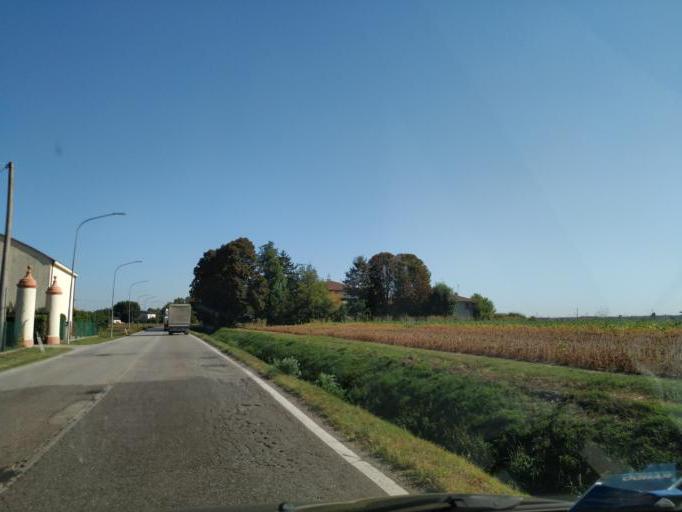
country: IT
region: Emilia-Romagna
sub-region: Provincia di Ferrara
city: Corpo Reno
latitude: 44.7622
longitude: 11.3175
